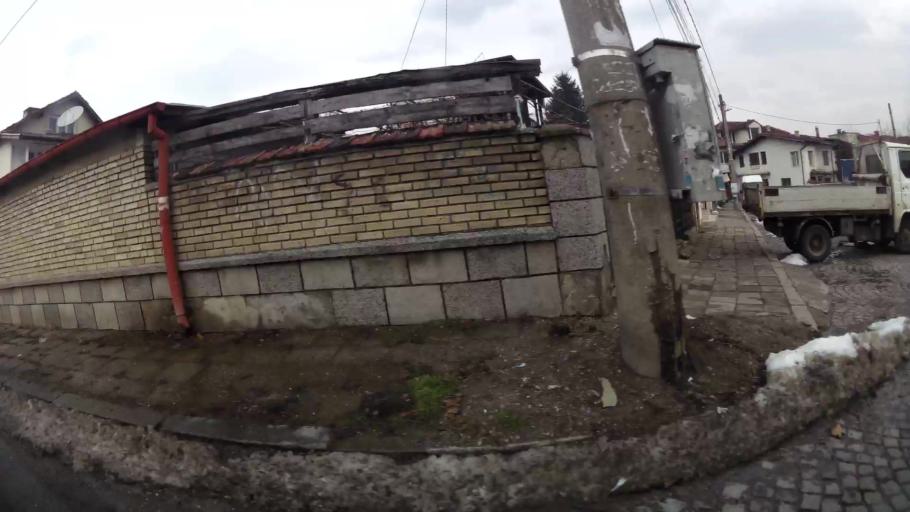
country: BG
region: Sofia-Capital
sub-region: Stolichna Obshtina
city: Sofia
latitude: 42.6613
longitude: 23.2426
